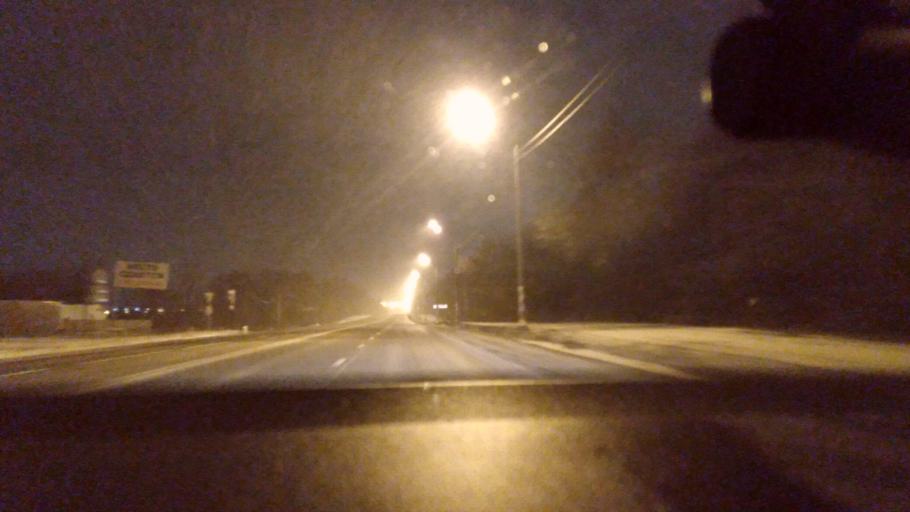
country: RU
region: Moskovskaya
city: Bronnitsy
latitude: 55.4784
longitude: 38.1812
